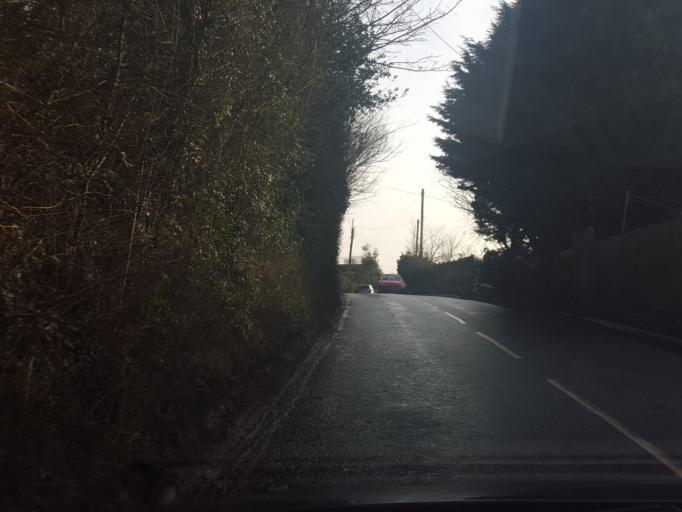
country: GB
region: England
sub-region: Suffolk
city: Sudbury
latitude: 51.9753
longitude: 0.7765
